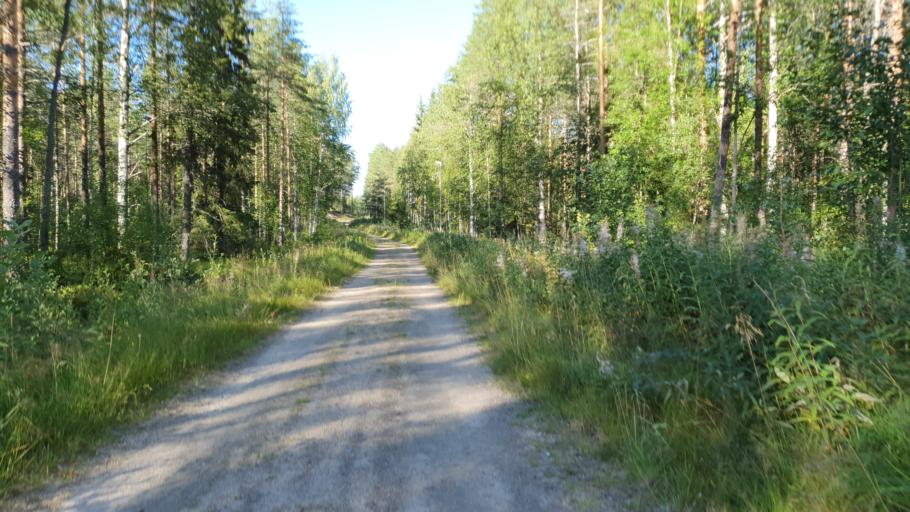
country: FI
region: Kainuu
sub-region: Kehys-Kainuu
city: Kuhmo
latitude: 64.1124
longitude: 29.5151
